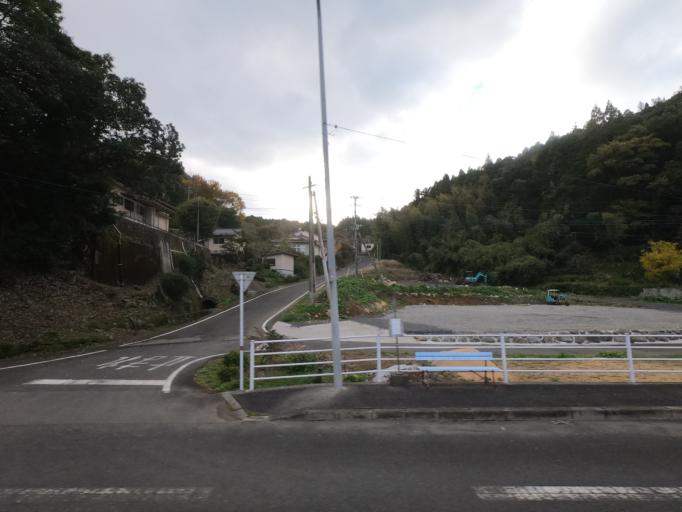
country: JP
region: Kumamoto
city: Minamata
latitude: 32.2640
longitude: 130.5073
